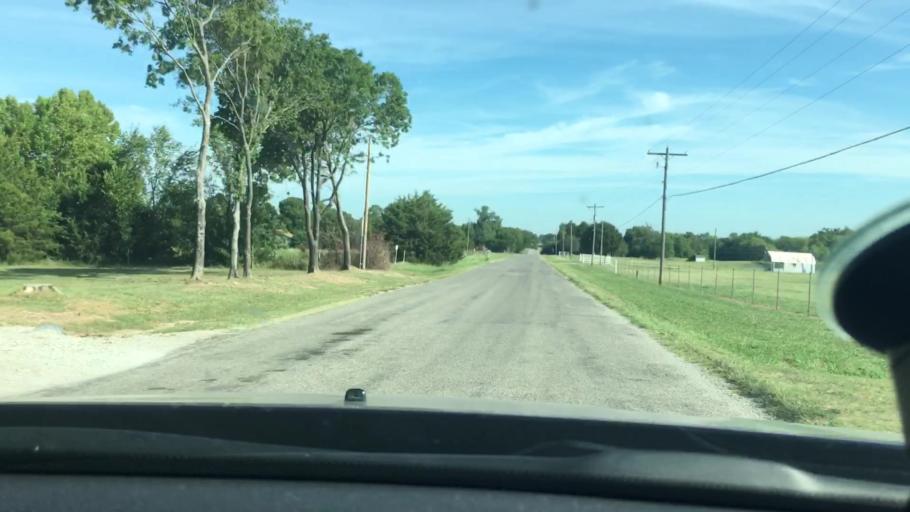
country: US
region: Oklahoma
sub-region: Carter County
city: Lone Grove
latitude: 34.2279
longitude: -97.2474
